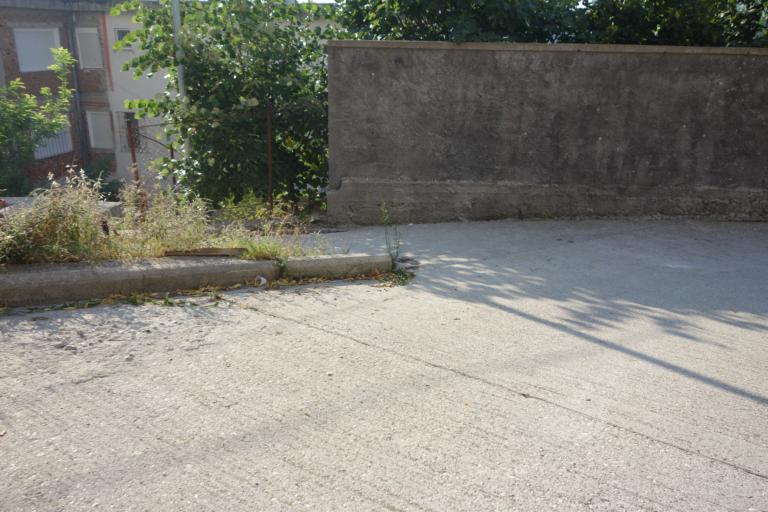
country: AL
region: Gjirokaster
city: Gjirokaster
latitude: 40.0804
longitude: 20.1447
